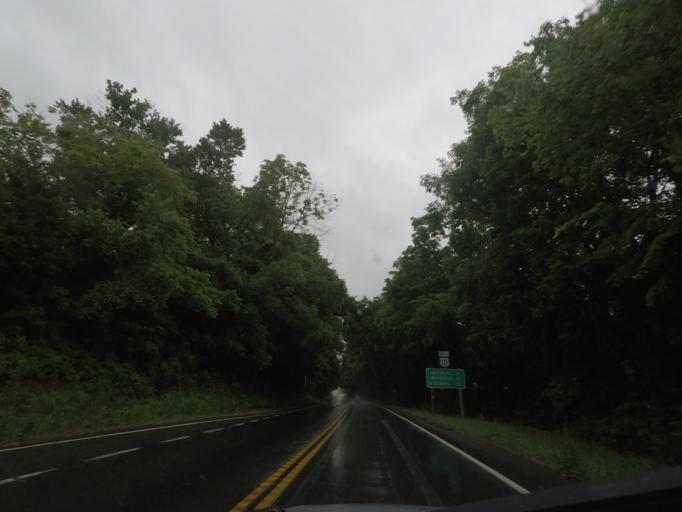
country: US
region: Virginia
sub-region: Orange County
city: Orange
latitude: 38.3505
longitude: -78.1152
